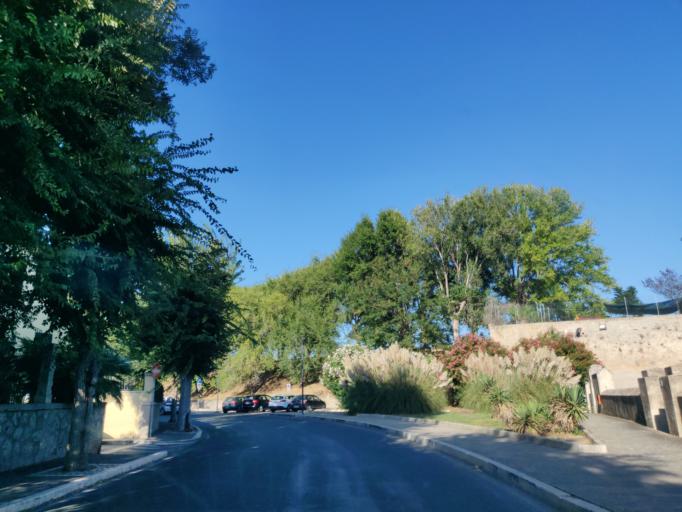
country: IT
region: Tuscany
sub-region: Provincia di Grosseto
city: Orbetello
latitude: 42.4373
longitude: 11.2138
